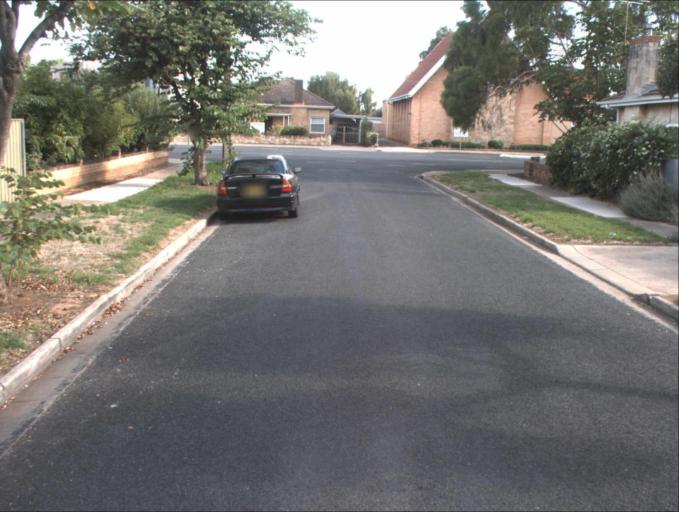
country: AU
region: South Australia
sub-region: Port Adelaide Enfield
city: Klemzig
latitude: -34.8724
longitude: 138.6217
